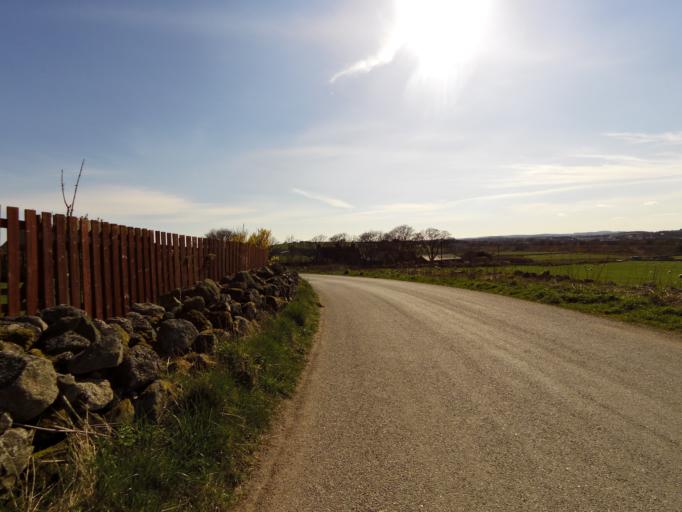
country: GB
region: Scotland
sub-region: Aberdeenshire
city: Portlethen
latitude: 57.0687
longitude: -2.1148
